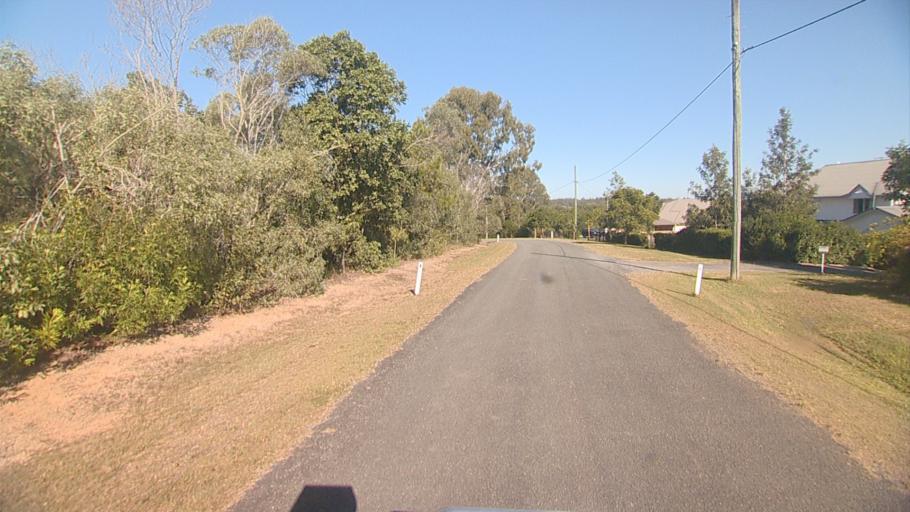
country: AU
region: Queensland
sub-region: Logan
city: Logan Reserve
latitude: -27.7437
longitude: 153.1234
